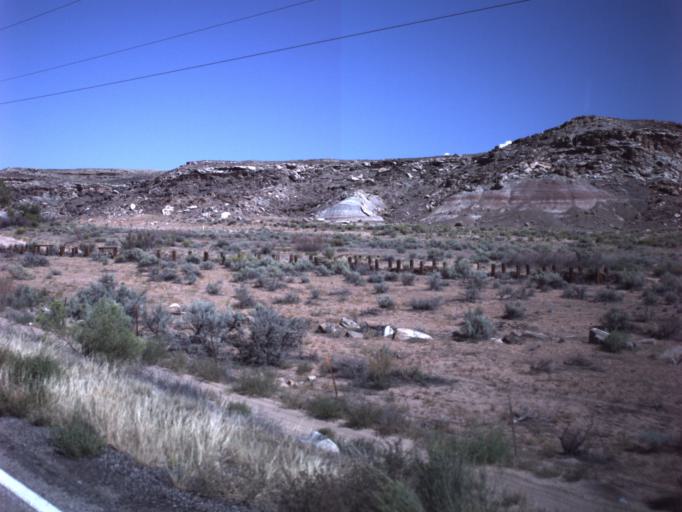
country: US
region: Utah
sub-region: Grand County
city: Moab
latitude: 38.7173
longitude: -109.7075
